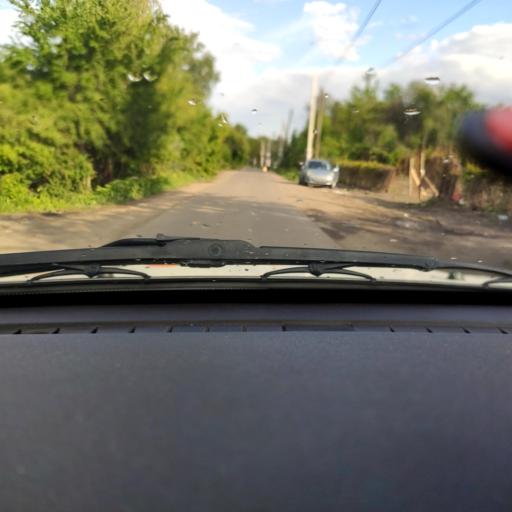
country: RU
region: Voronezj
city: Shilovo
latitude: 51.5848
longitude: 39.1599
